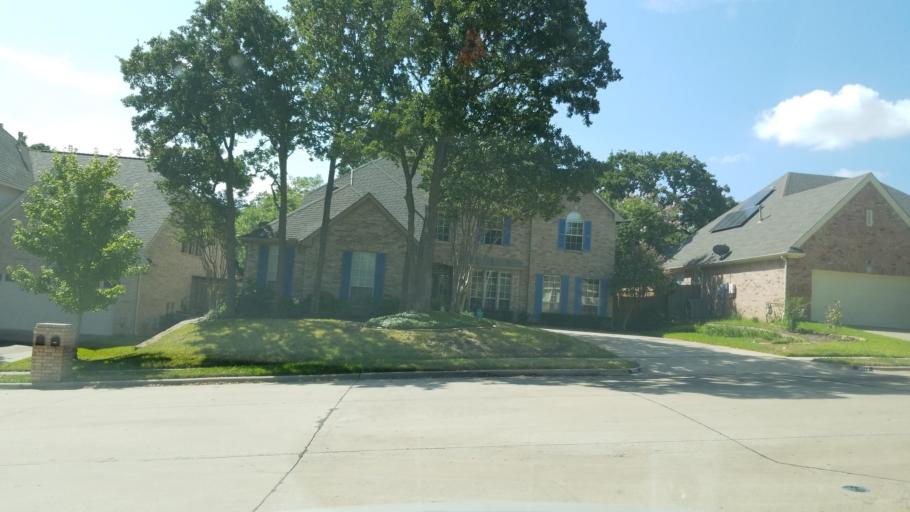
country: US
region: Texas
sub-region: Tarrant County
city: Euless
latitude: 32.8598
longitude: -97.1021
